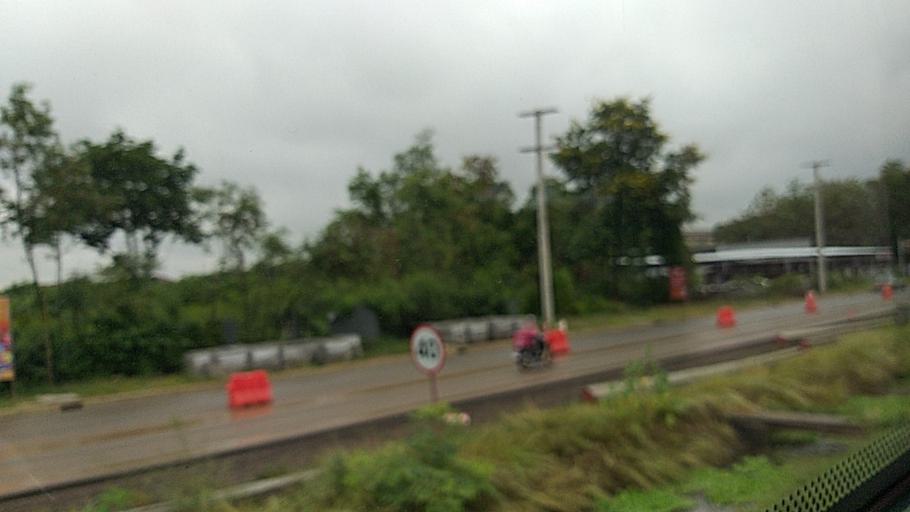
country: TH
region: Nakhon Ratchasima
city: Nakhon Ratchasima
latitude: 14.9951
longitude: 102.0710
